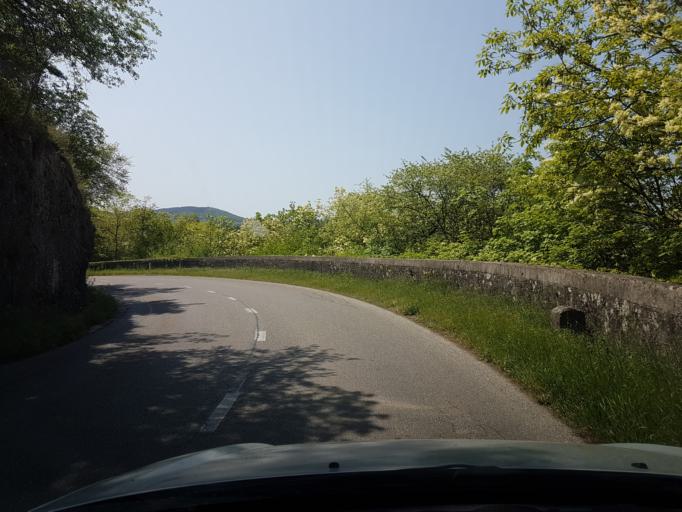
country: SI
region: Komen
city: Komen
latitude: 45.7996
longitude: 13.7102
